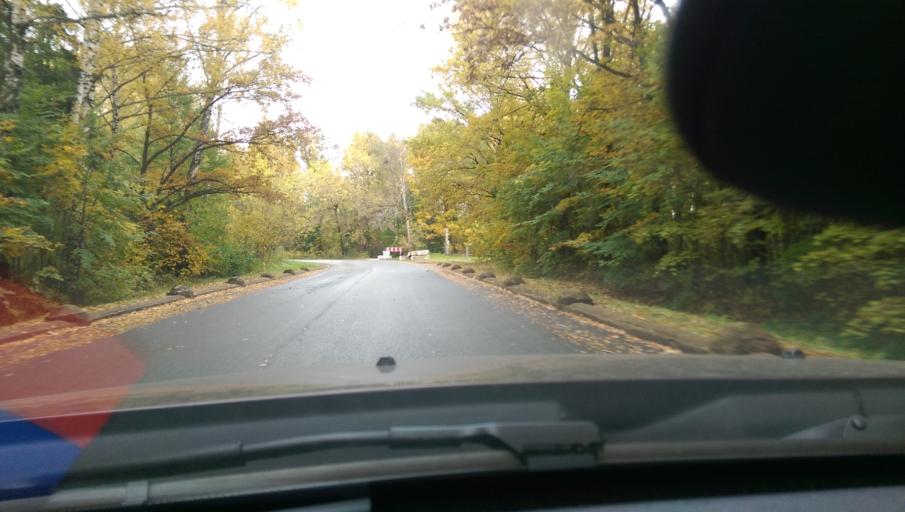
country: RU
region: Moskovskaya
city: Pirogovskiy
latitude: 56.0307
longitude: 37.7147
